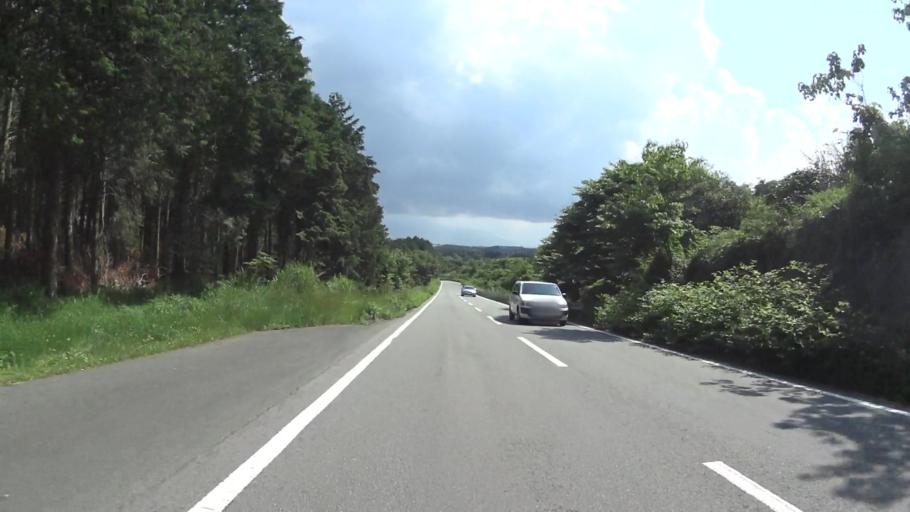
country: JP
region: Kumamoto
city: Aso
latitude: 33.0486
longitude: 131.1683
